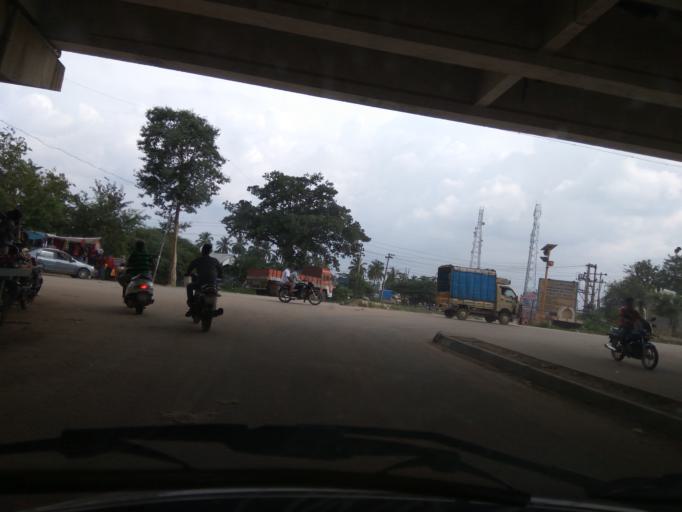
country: IN
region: Karnataka
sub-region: Kolar
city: Kolar
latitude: 13.1259
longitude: 78.1134
